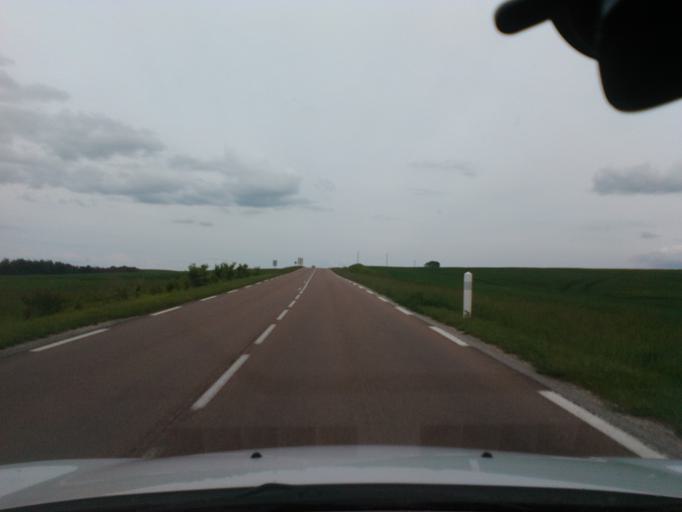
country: FR
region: Champagne-Ardenne
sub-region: Departement de l'Aube
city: Ville-sous-la-Ferte
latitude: 48.2170
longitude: 4.8224
